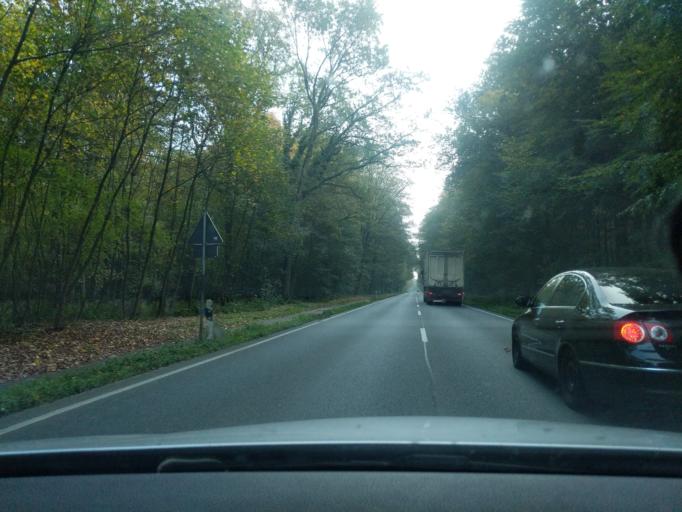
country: DE
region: Lower Saxony
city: Himmelpforten
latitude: 53.6056
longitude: 9.3180
